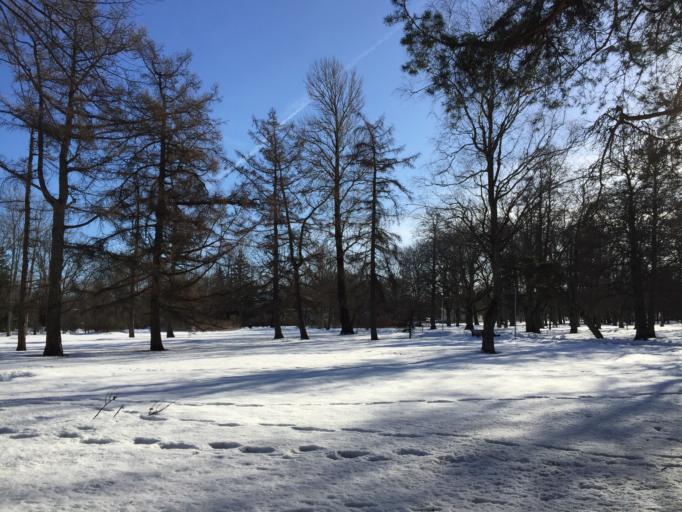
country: EE
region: Paernumaa
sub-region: Paernu linn
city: Parnu
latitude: 58.3798
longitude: 24.4910
